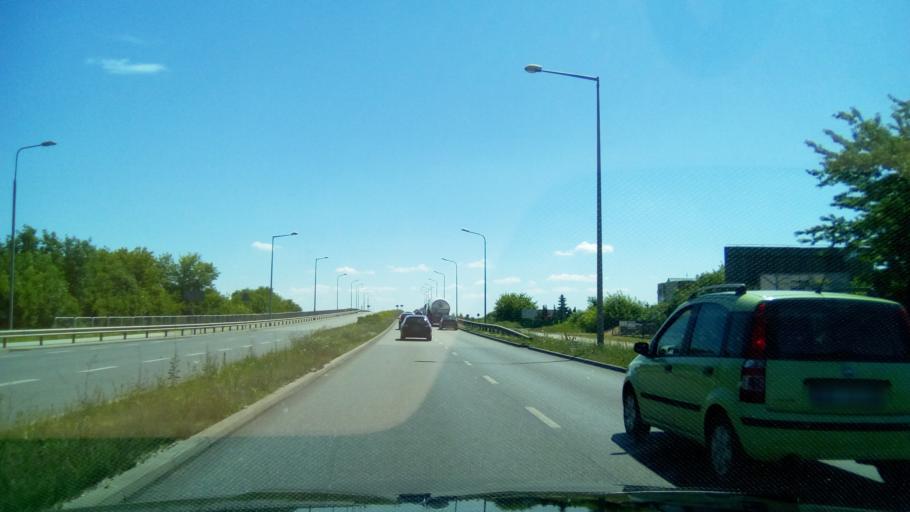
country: PL
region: Masovian Voivodeship
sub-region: Radom
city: Radom
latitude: 51.4208
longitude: 21.1808
